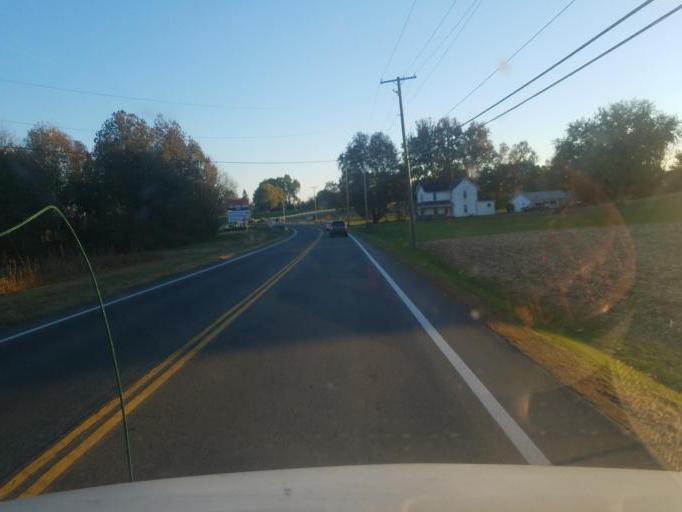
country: US
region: Ohio
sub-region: Licking County
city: Newark
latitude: 40.1232
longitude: -82.4296
